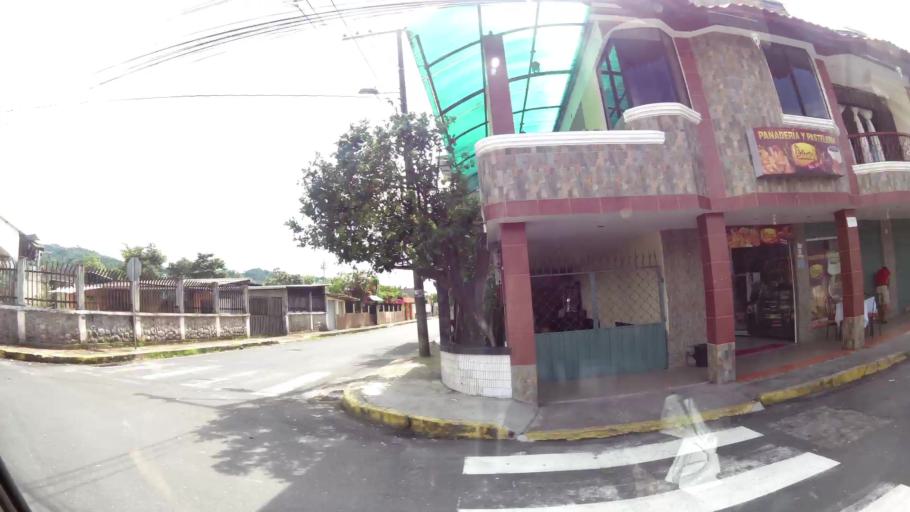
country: EC
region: Pastaza
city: Puyo
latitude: -1.4992
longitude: -78.0610
